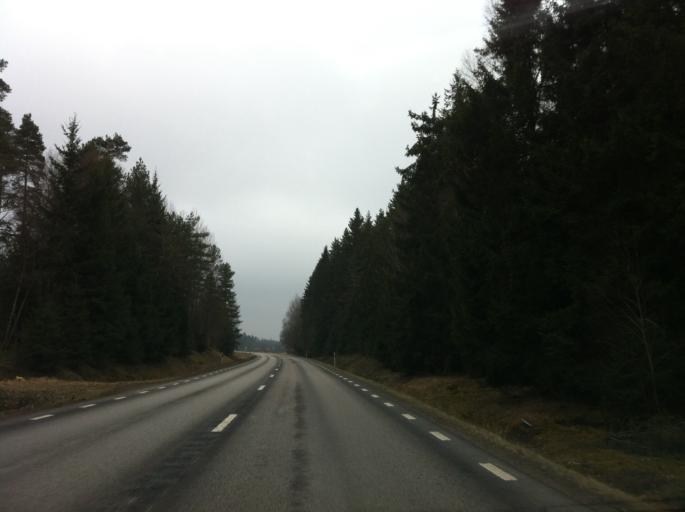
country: SE
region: Vaestra Goetaland
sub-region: Boras Kommun
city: Ganghester
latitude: 57.6704
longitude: 13.0502
